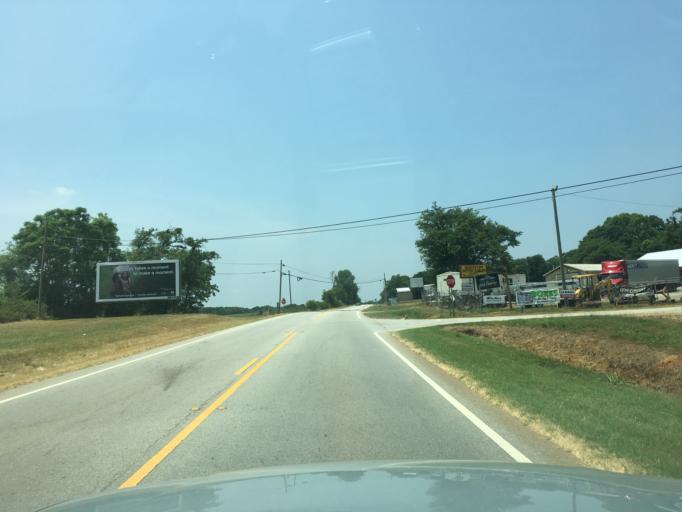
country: US
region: Georgia
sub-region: Hart County
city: Royston
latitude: 34.2885
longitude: -83.0891
